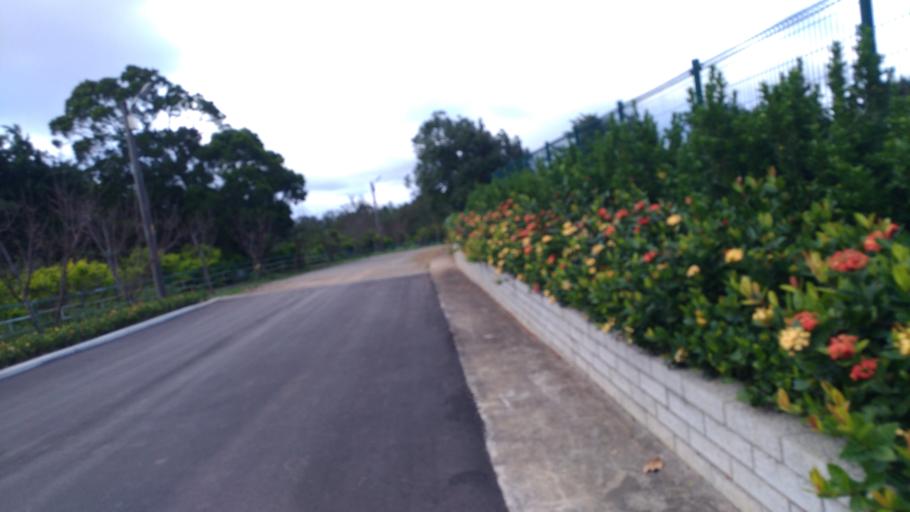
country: TW
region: Taiwan
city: Daxi
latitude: 24.8878
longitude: 121.1714
